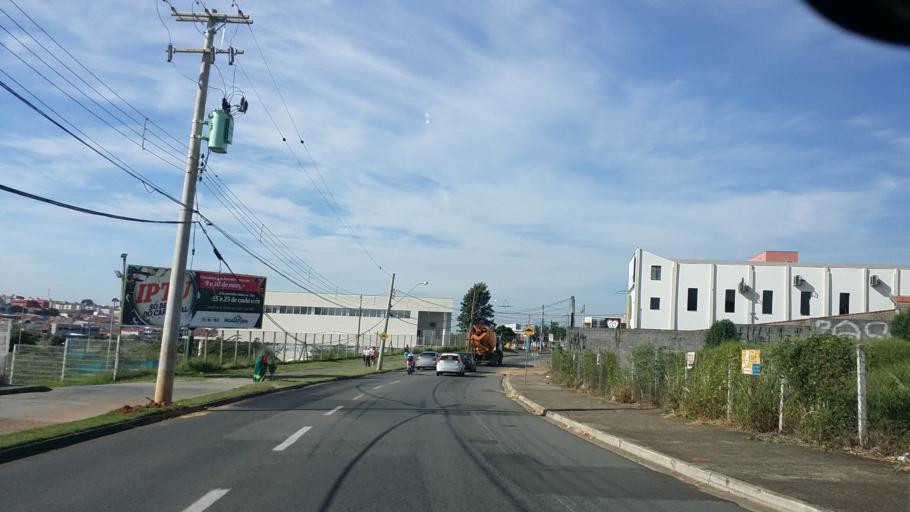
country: BR
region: Sao Paulo
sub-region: Indaiatuba
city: Indaiatuba
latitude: -23.0990
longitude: -47.2288
